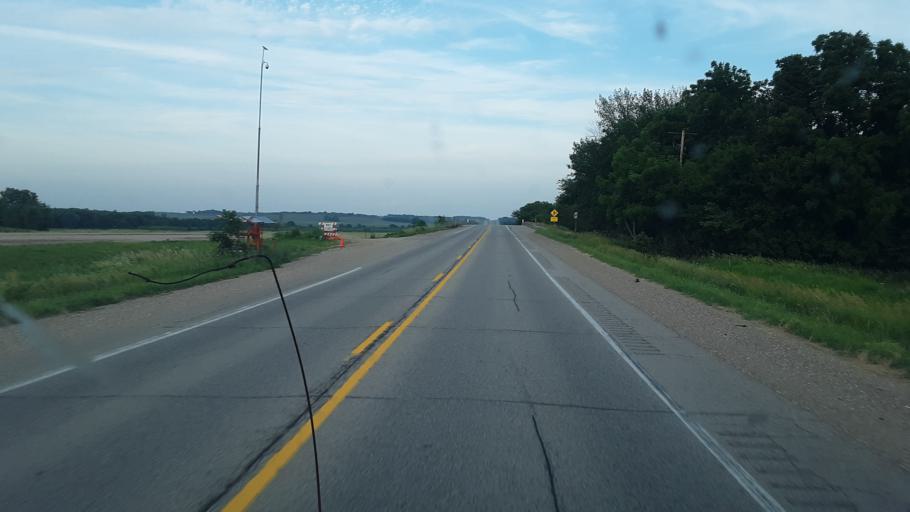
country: US
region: Iowa
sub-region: Tama County
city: Tama
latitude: 41.9638
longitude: -92.4991
